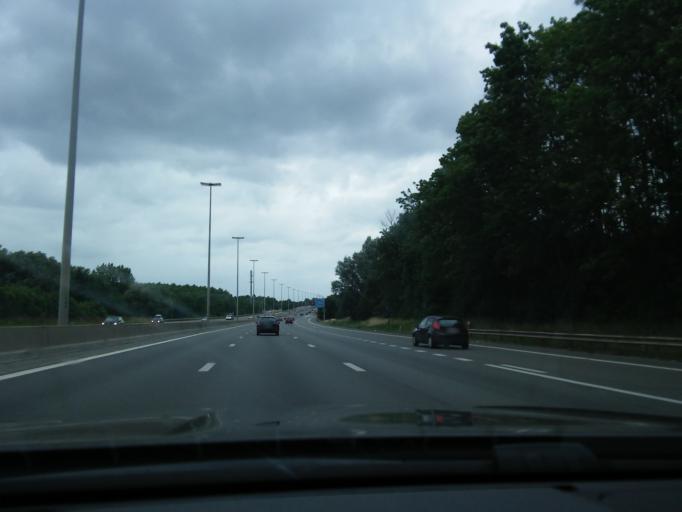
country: BE
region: Flanders
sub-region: Provincie Vlaams-Brabant
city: Dilbeek
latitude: 50.8591
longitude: 4.2718
